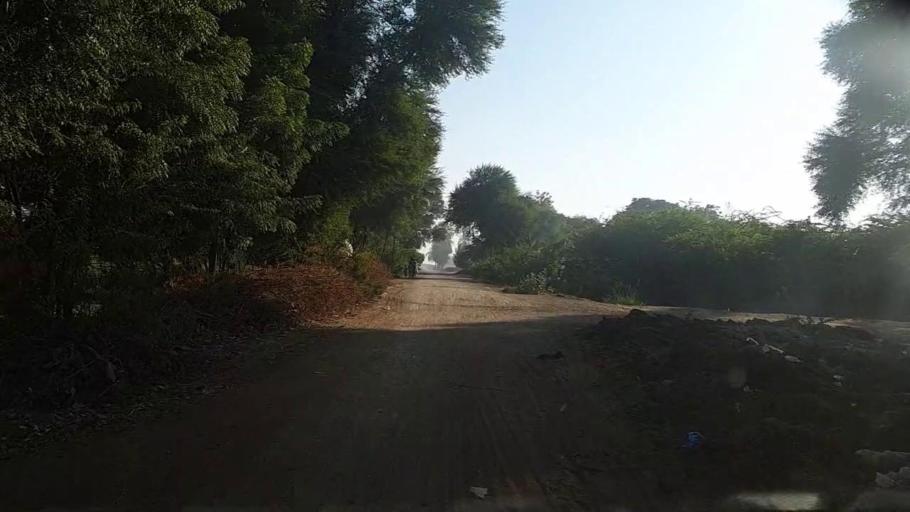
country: PK
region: Sindh
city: Darya Khan Marri
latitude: 26.6958
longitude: 68.3625
